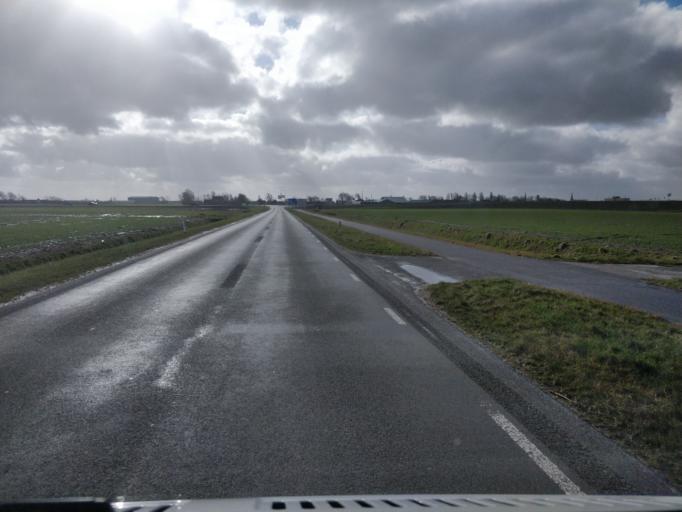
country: NL
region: Friesland
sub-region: Gemeente Harlingen
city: Harlingen
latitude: 53.1877
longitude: 5.4406
